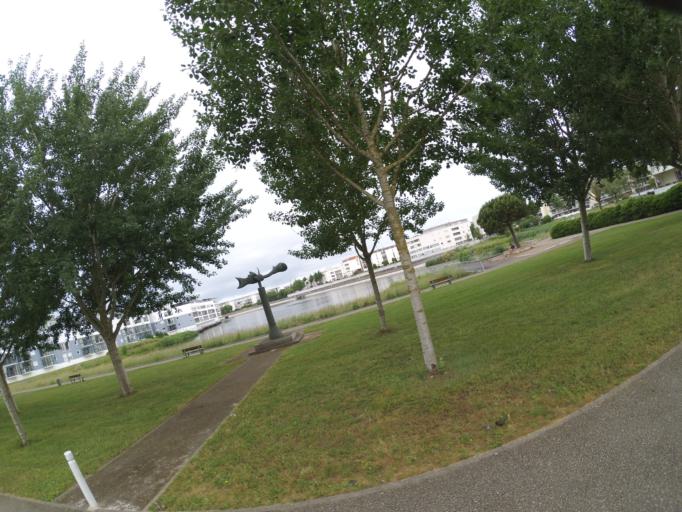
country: FR
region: Poitou-Charentes
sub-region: Departement de la Charente-Maritime
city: La Rochelle
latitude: 46.1448
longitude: -1.1526
